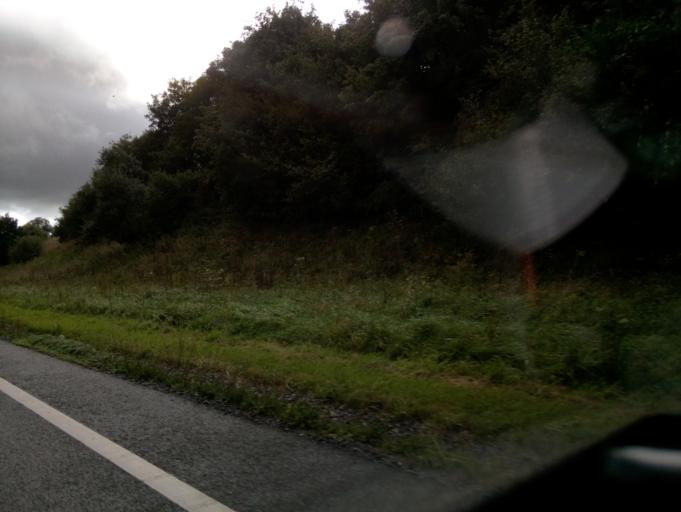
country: GB
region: England
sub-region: Devon
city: South Brent
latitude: 50.4046
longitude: -3.8527
